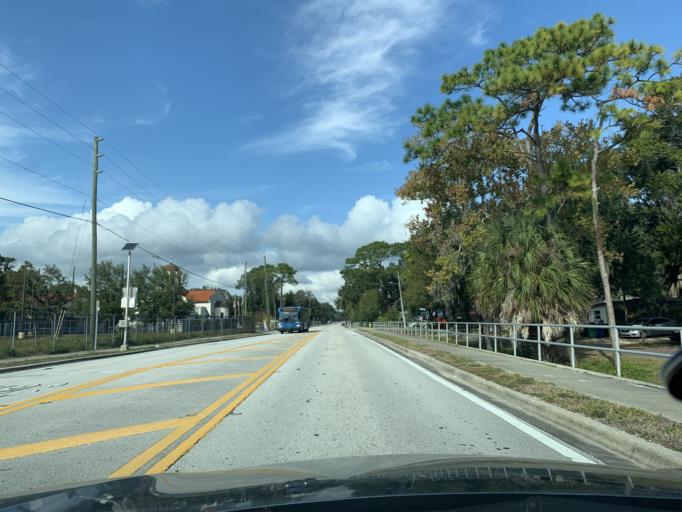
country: US
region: Florida
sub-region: Pinellas County
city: South Highpoint
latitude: 27.9098
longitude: -82.7129
